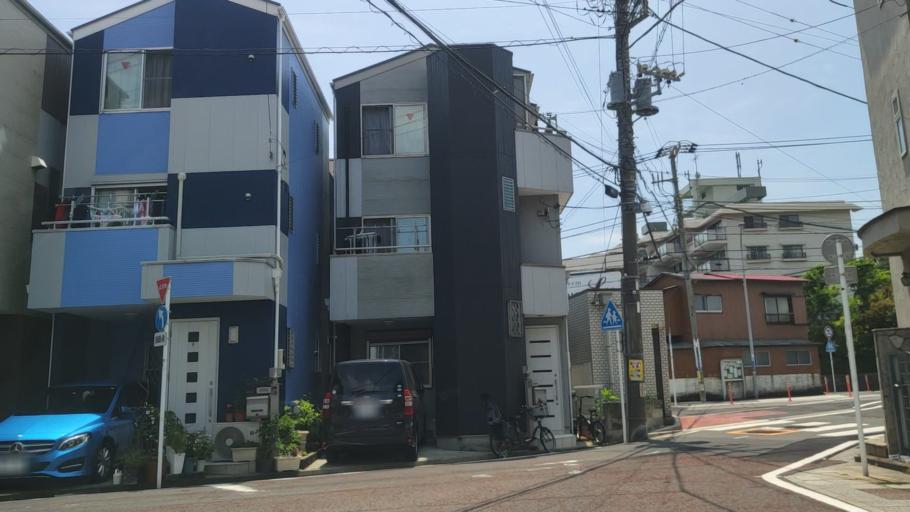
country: JP
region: Kanagawa
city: Yokohama
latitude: 35.4198
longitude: 139.6642
